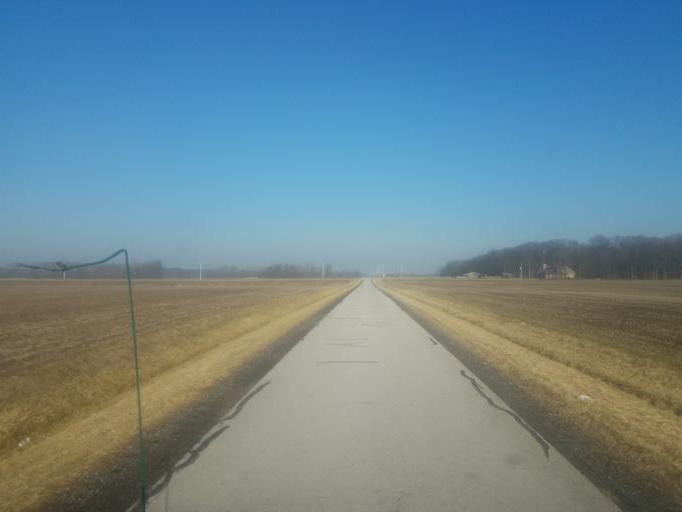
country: US
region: Ohio
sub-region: Seneca County
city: Tiffin
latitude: 41.0489
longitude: -83.1129
